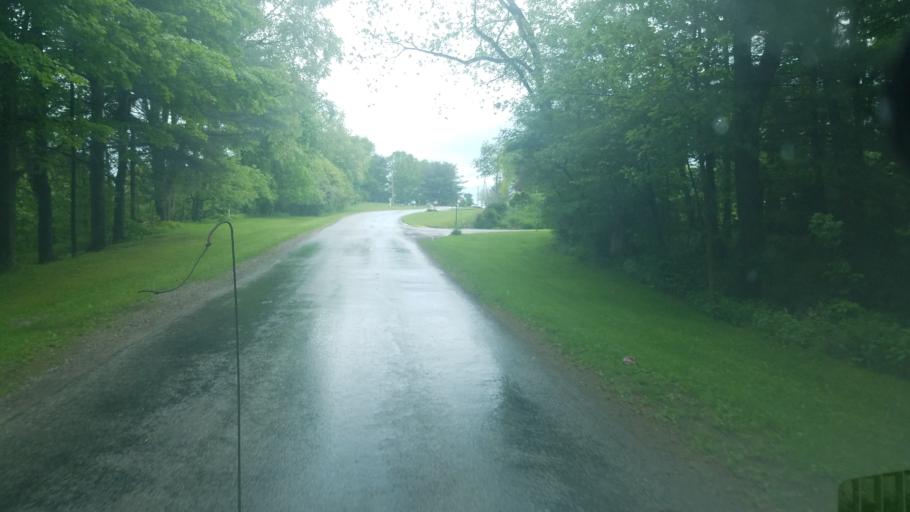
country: US
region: Ohio
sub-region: Wayne County
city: Smithville
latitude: 40.8269
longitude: -81.8753
